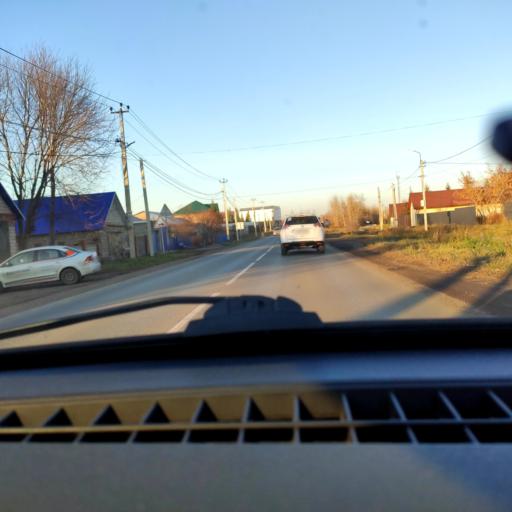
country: RU
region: Bashkortostan
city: Ufa
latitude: 54.6199
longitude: 55.9065
